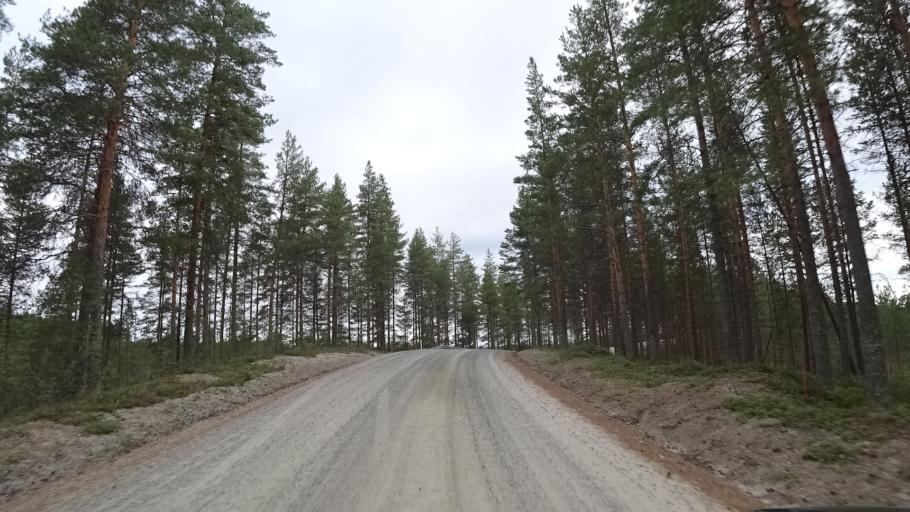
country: FI
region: North Karelia
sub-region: Pielisen Karjala
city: Lieksa
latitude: 63.2580
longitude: 30.3195
